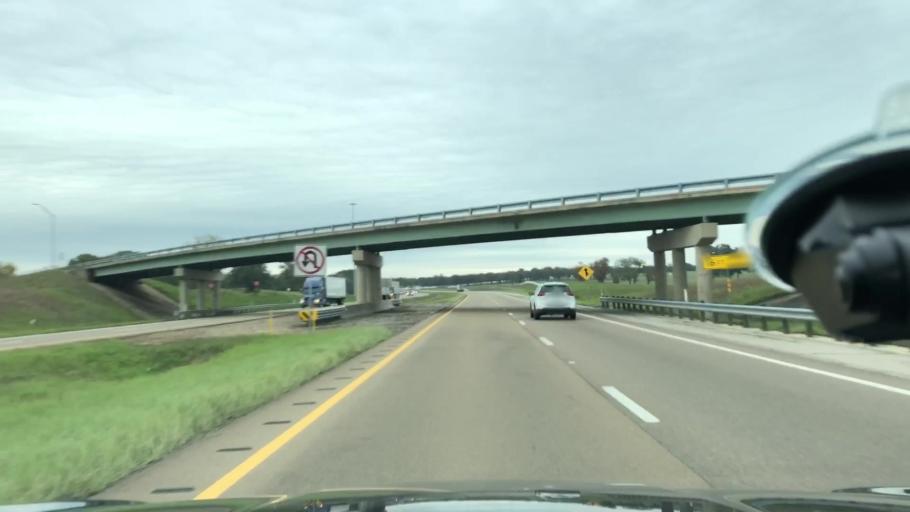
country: US
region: Texas
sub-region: Titus County
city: Mount Pleasant
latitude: 33.1978
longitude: -94.9206
